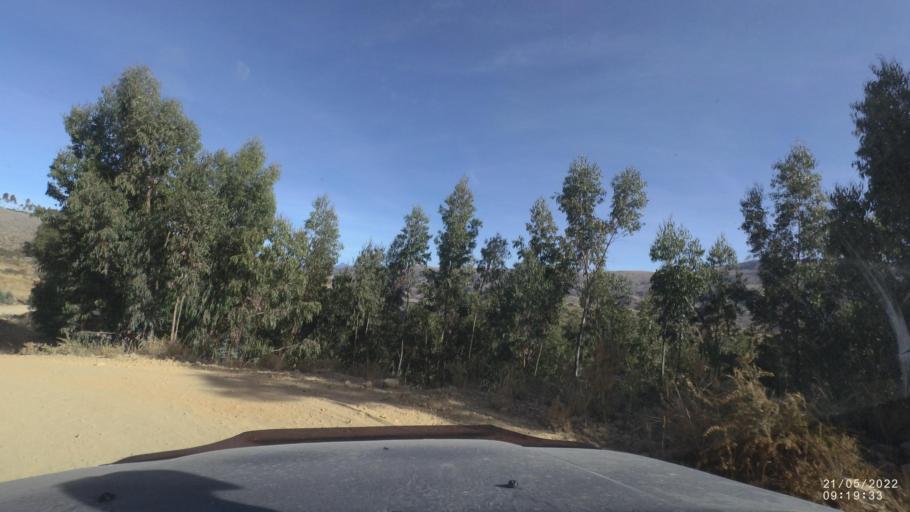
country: BO
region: Cochabamba
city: Cochabamba
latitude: -17.3572
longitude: -66.0207
